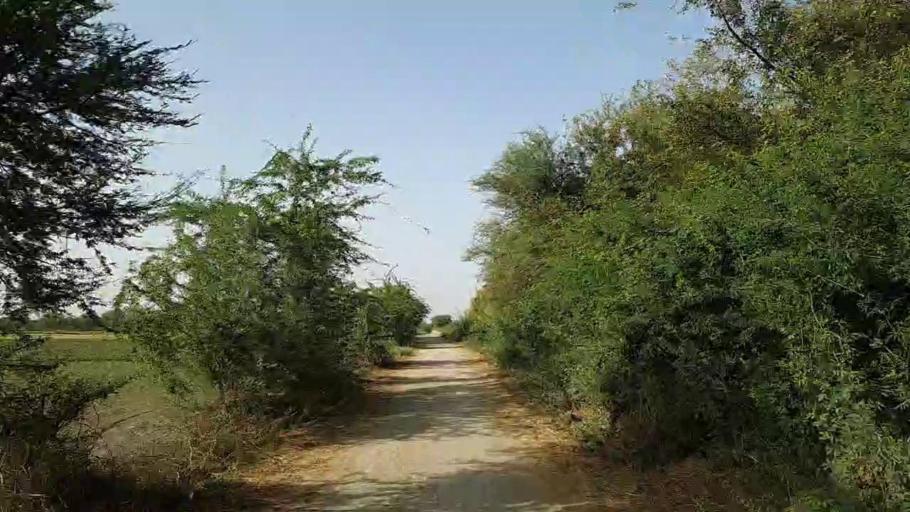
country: PK
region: Sindh
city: Jati
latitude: 24.2858
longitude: 68.1492
